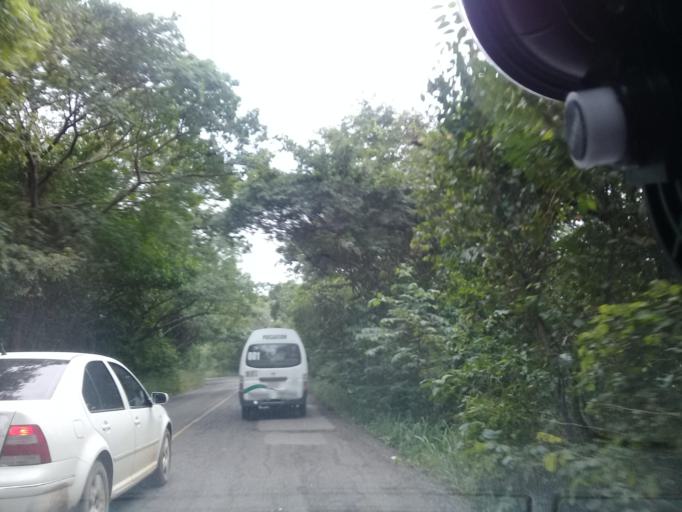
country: MX
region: Veracruz
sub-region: Chalma
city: San Pedro Coyutla
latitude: 21.2023
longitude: -98.3894
